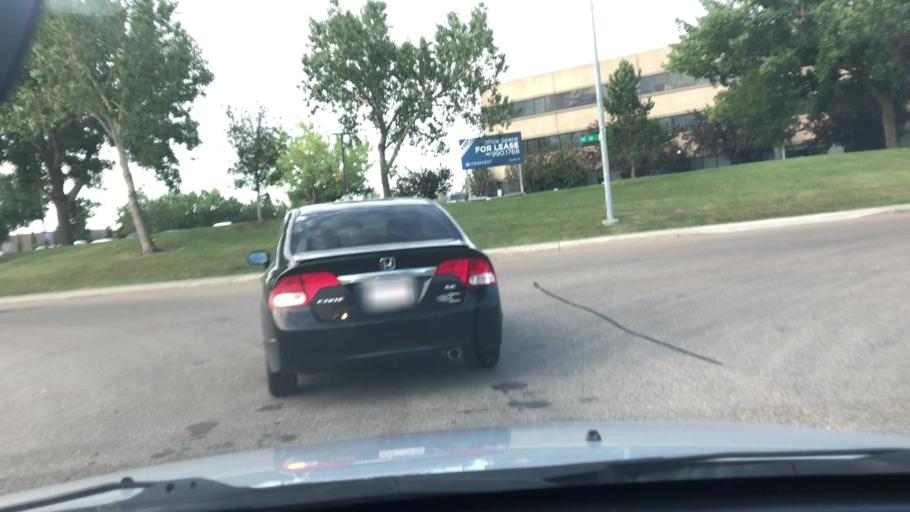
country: CA
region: Alberta
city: Edmonton
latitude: 53.5375
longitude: -113.4150
